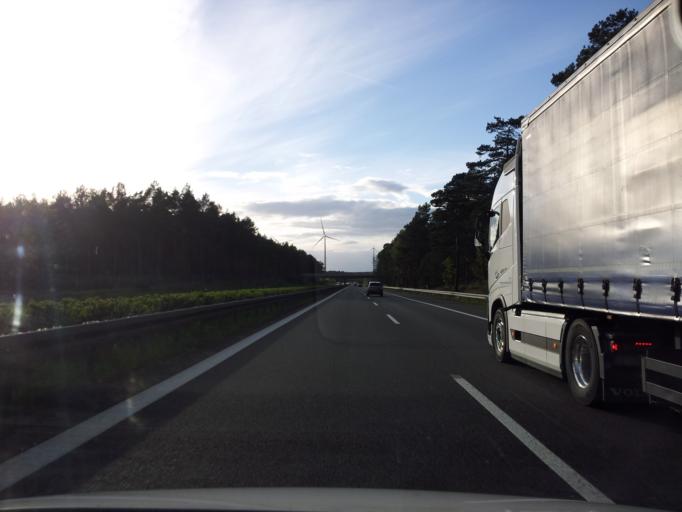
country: DE
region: Brandenburg
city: Vetschau
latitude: 51.7508
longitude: 14.1371
